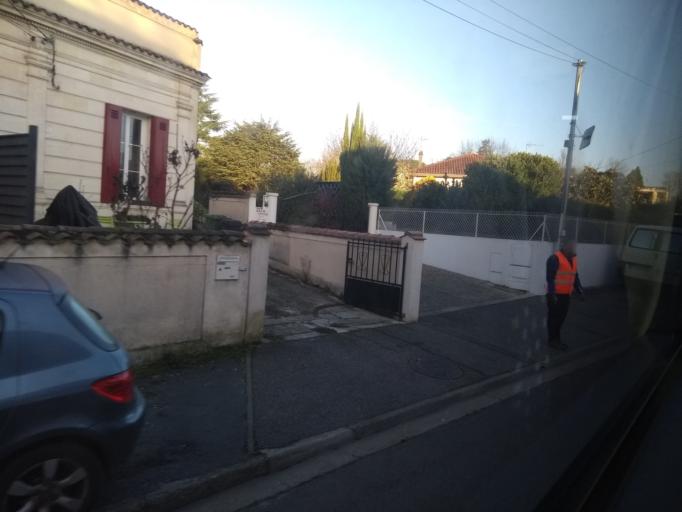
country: FR
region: Aquitaine
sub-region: Departement de la Gironde
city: Gradignan
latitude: 44.7695
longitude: -0.6165
